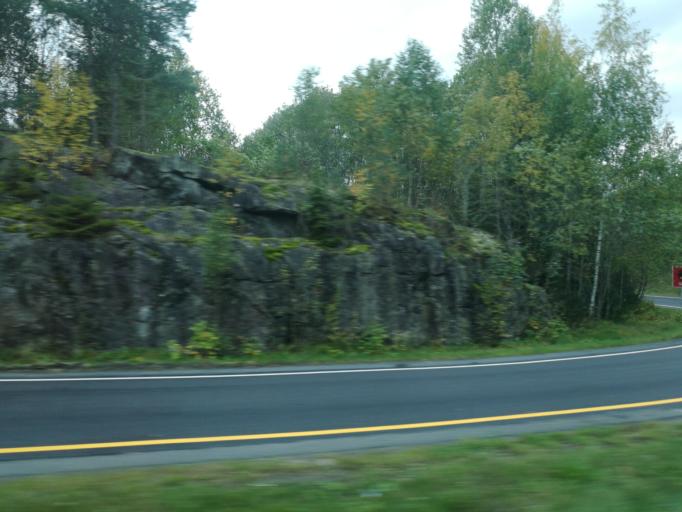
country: NO
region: Akershus
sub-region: Lorenskog
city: Kjenn
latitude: 59.9321
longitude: 10.9464
